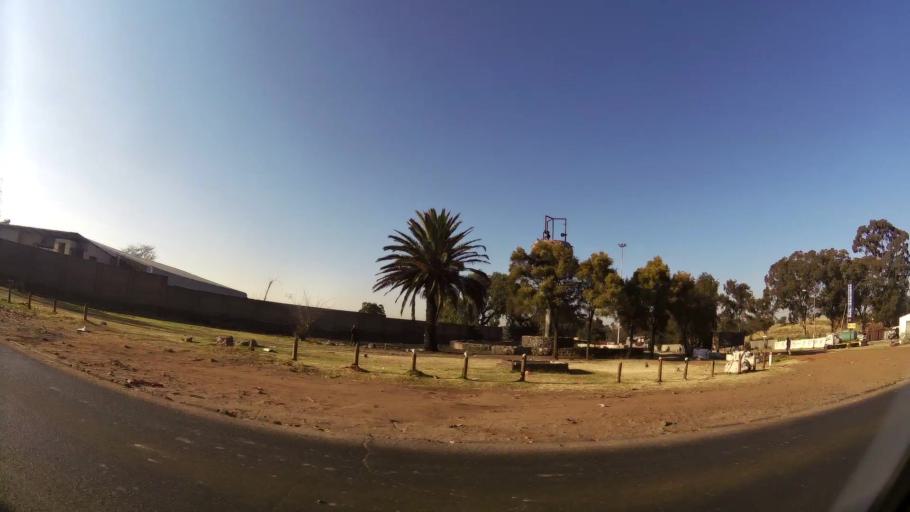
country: ZA
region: Gauteng
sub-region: Ekurhuleni Metropolitan Municipality
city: Germiston
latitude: -26.1991
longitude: 28.1488
